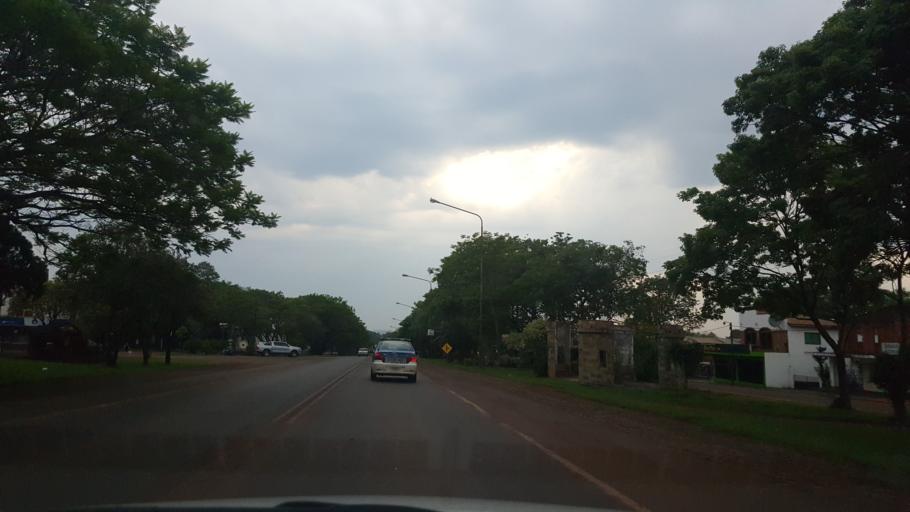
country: AR
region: Misiones
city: Jardin America
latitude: -27.0462
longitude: -55.2408
